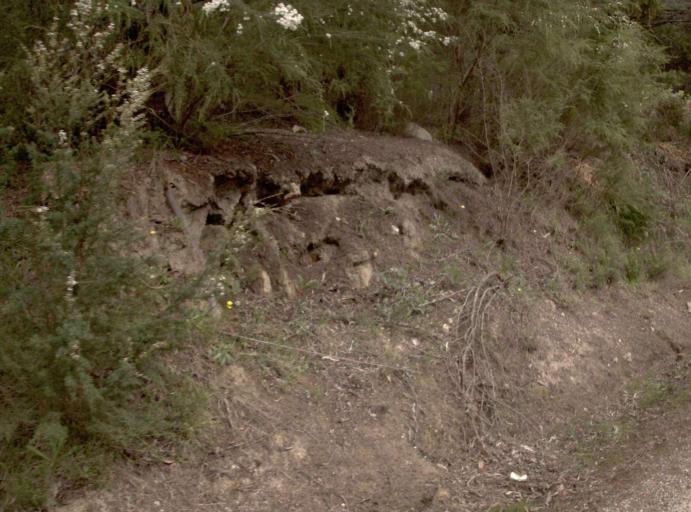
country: AU
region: New South Wales
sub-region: Bombala
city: Bombala
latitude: -37.4279
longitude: 149.1991
